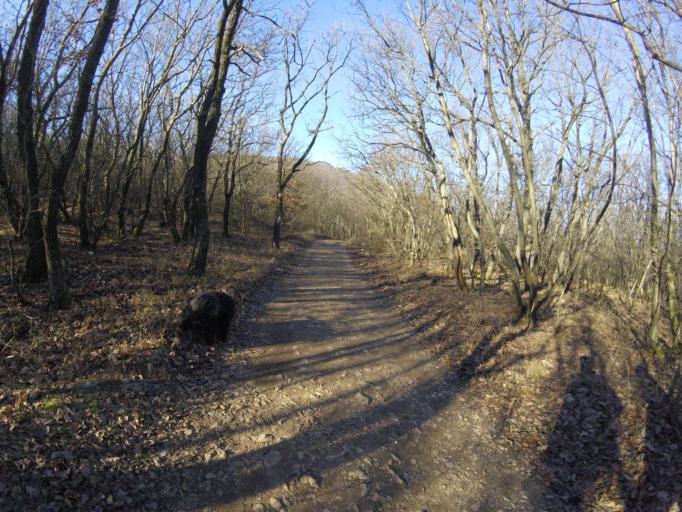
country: HU
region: Pest
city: Pilisszanto
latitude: 47.6830
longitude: 18.8915
